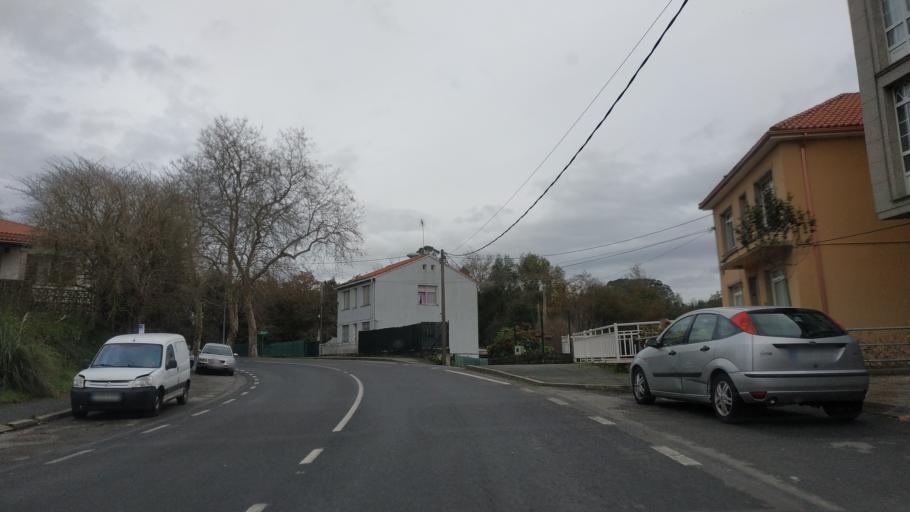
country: ES
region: Galicia
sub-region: Provincia da Coruna
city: Oleiros
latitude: 43.3496
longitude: -8.3419
